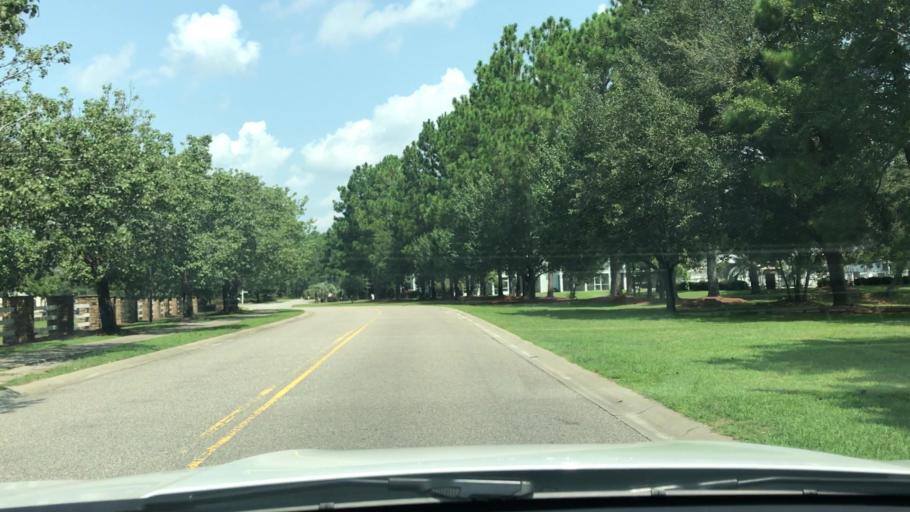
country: US
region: South Carolina
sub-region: Horry County
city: Forestbrook
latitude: 33.7802
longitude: -78.9656
